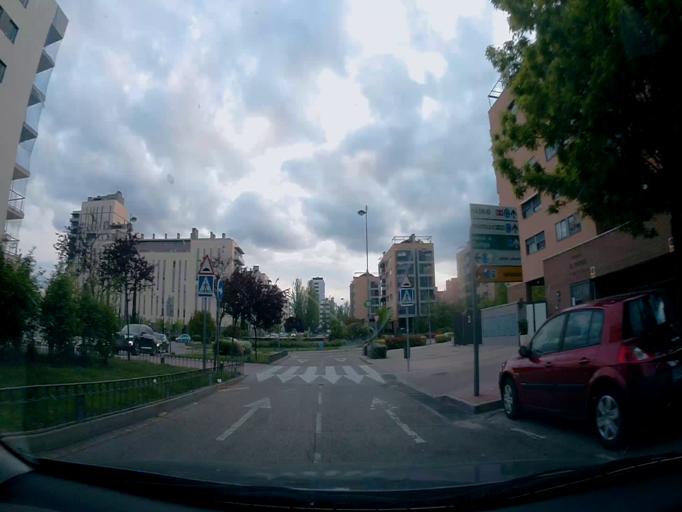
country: ES
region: Madrid
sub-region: Provincia de Madrid
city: Alcorcon
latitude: 40.3438
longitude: -3.8434
